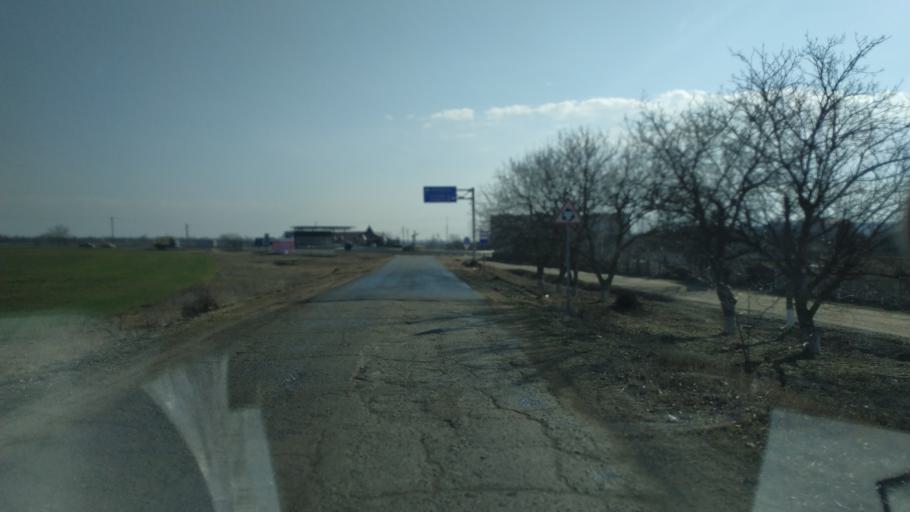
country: MD
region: Chisinau
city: Singera
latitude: 46.6880
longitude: 29.0503
